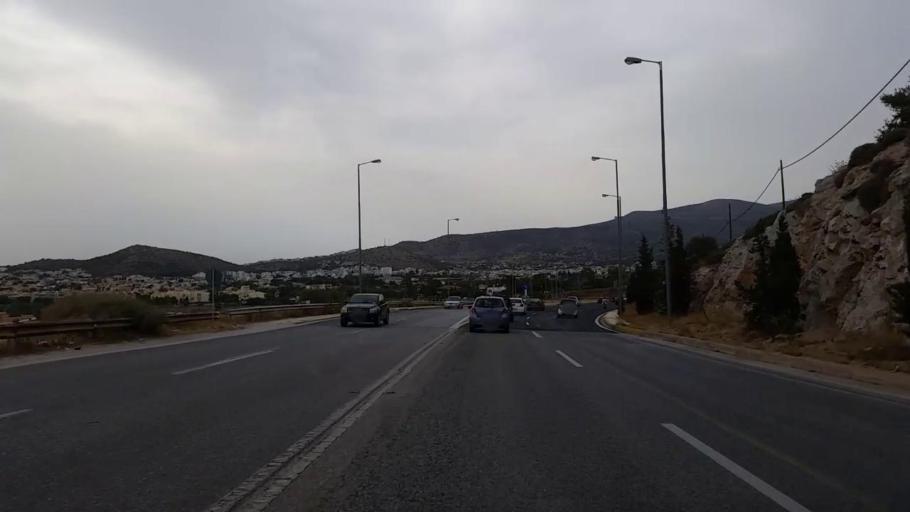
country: GR
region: Attica
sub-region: Nomarchia Anatolikis Attikis
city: Vari
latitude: 37.8198
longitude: 23.8179
